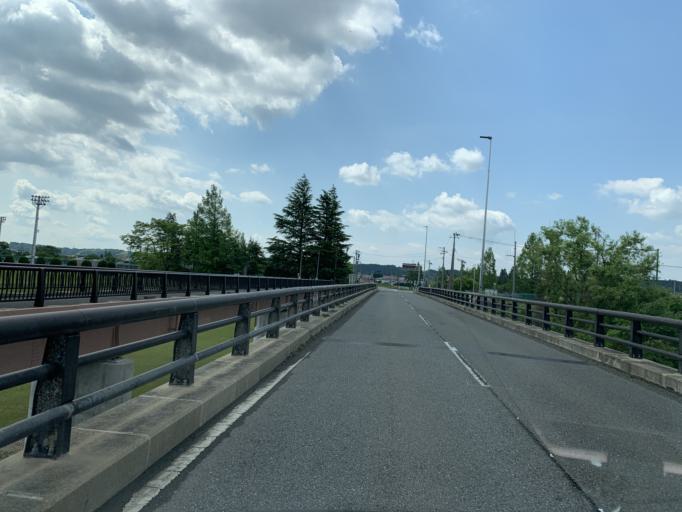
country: JP
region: Miyagi
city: Furukawa
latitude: 38.7461
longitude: 140.9539
